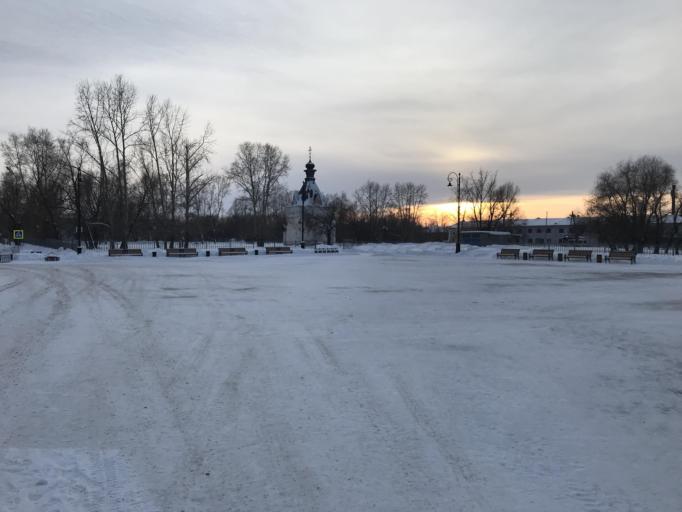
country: RU
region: Tjumen
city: Tobol'sk
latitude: 58.1936
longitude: 68.2438
